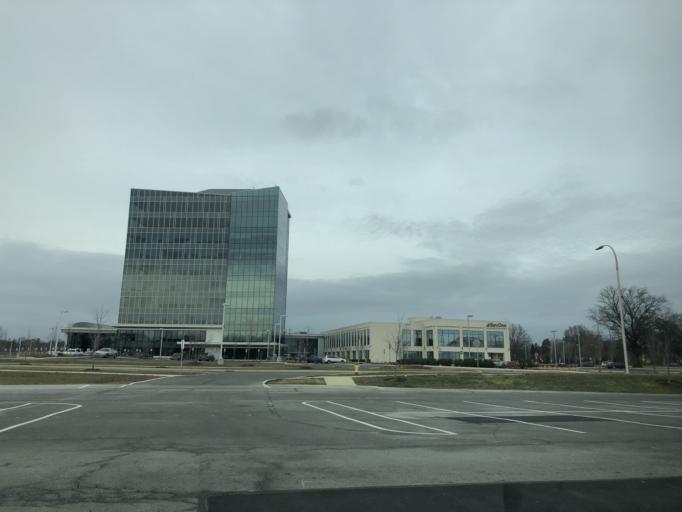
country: US
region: Delaware
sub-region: New Castle County
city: Newark
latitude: 39.6627
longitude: -75.7535
